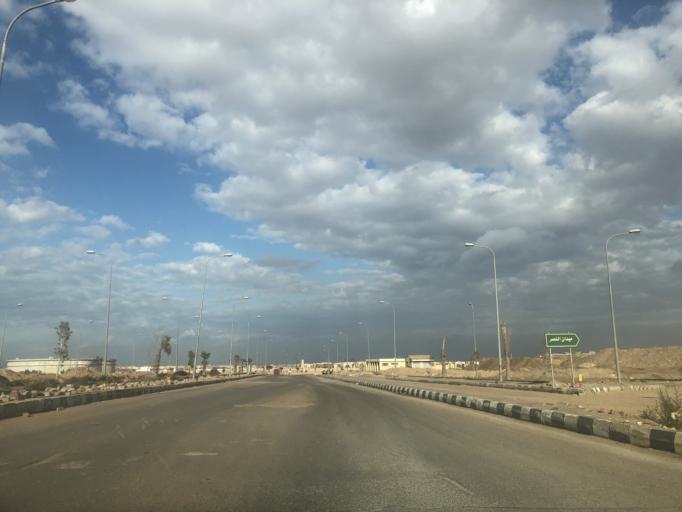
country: EG
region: Al Jizah
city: Madinat Sittah Uktubar
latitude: 29.9277
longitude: 31.0358
